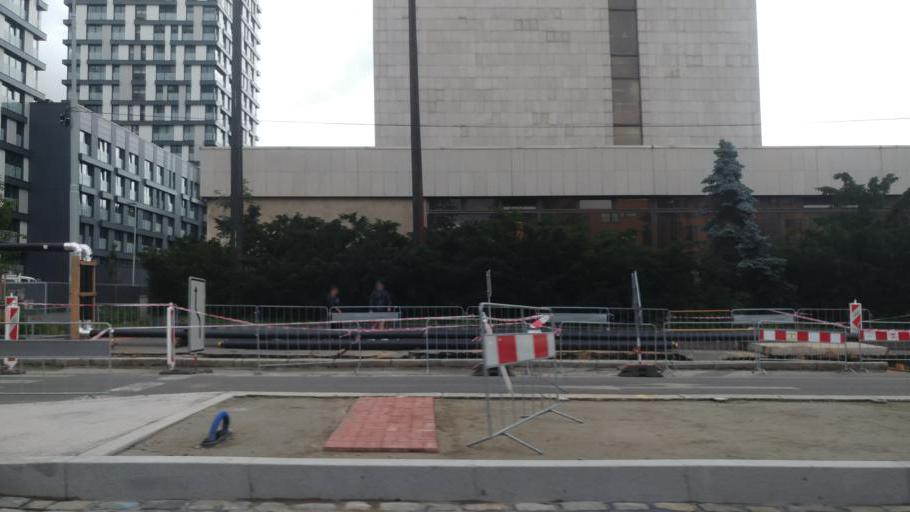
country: CZ
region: Praha
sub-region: Praha 8
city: Karlin
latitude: 50.0835
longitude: 14.4654
